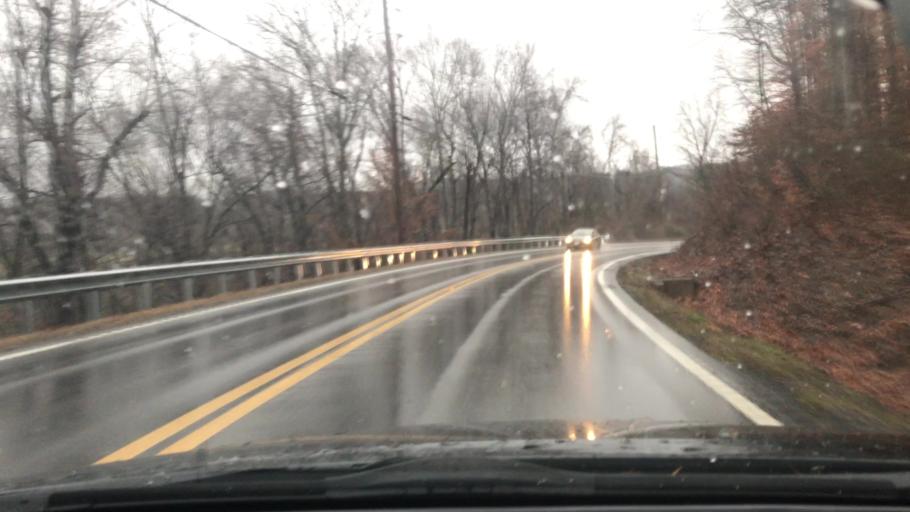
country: US
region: Tennessee
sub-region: Cheatham County
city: Ashland City
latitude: 36.2821
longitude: -87.1085
